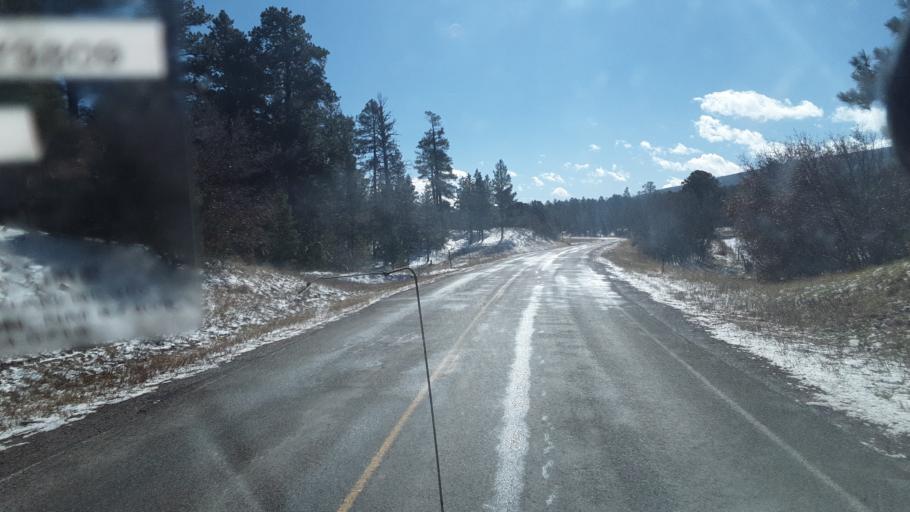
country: US
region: New Mexico
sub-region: Rio Arriba County
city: Santa Teresa
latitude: 36.2085
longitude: -106.7754
